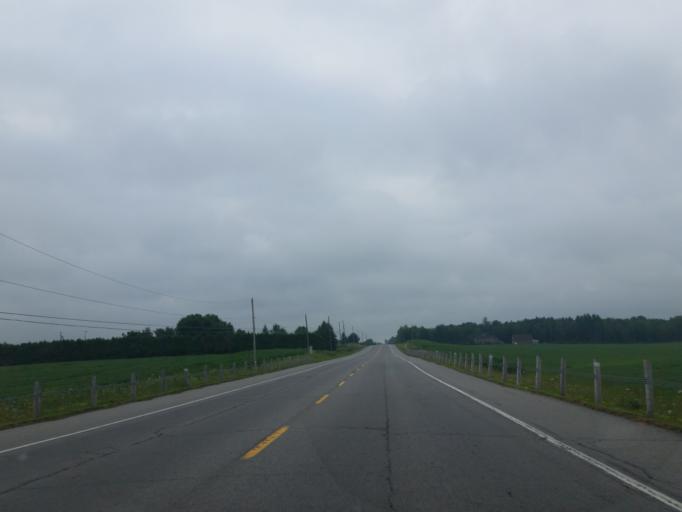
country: CA
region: Ontario
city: Clarence-Rockland
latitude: 45.3971
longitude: -75.3944
